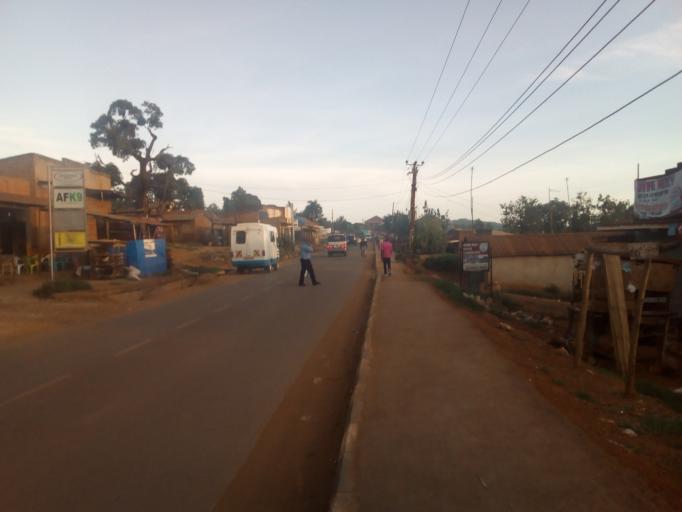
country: UG
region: Central Region
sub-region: Wakiso District
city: Kajansi
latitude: 0.2441
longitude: 32.5721
